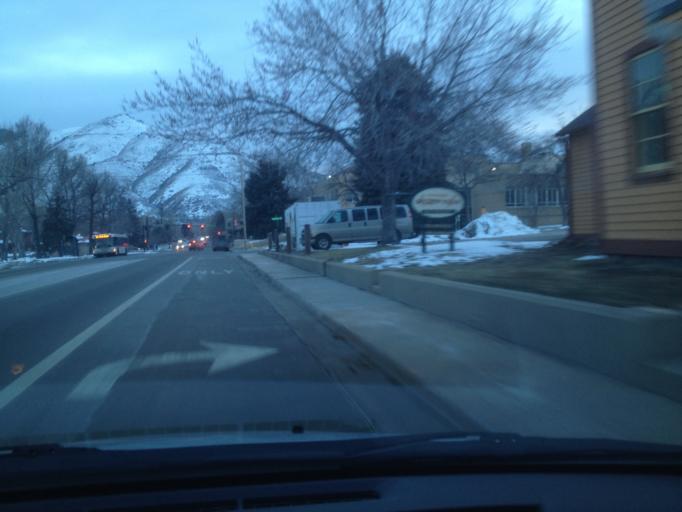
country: US
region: Colorado
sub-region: Jefferson County
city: Golden
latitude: 39.7587
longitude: -105.2215
